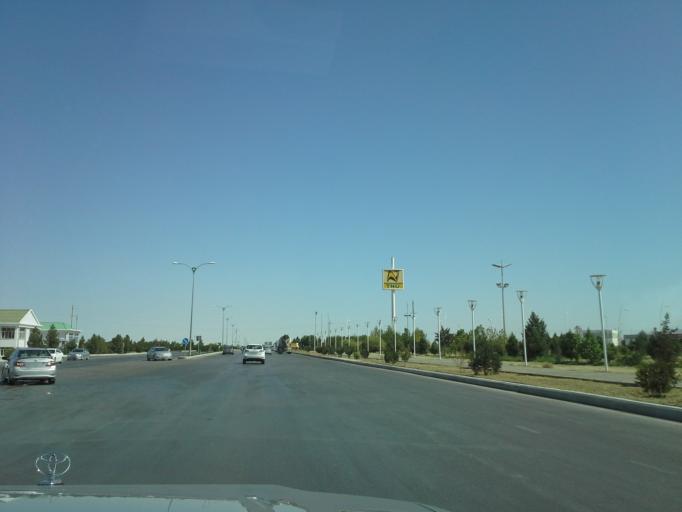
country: TM
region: Ahal
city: Annau
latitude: 37.9073
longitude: 58.5146
